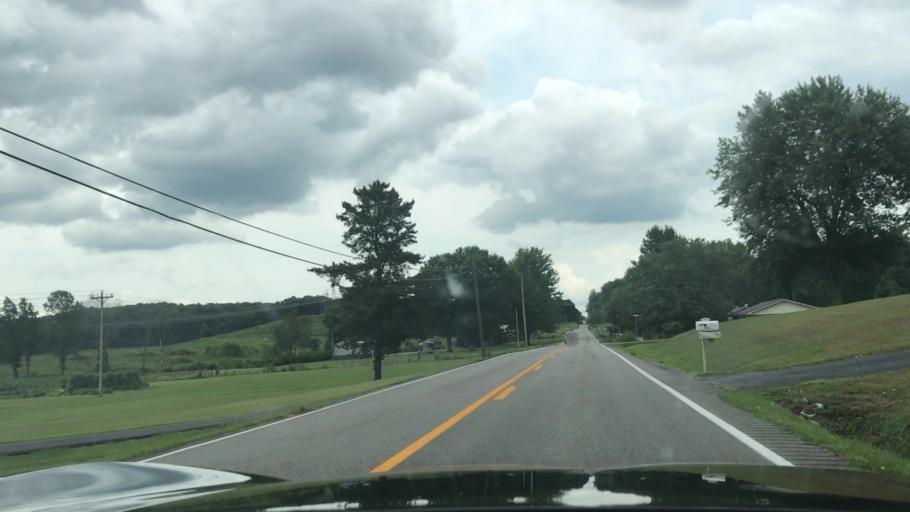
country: US
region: Kentucky
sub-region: Muhlenberg County
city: Central City
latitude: 37.2014
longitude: -87.0077
